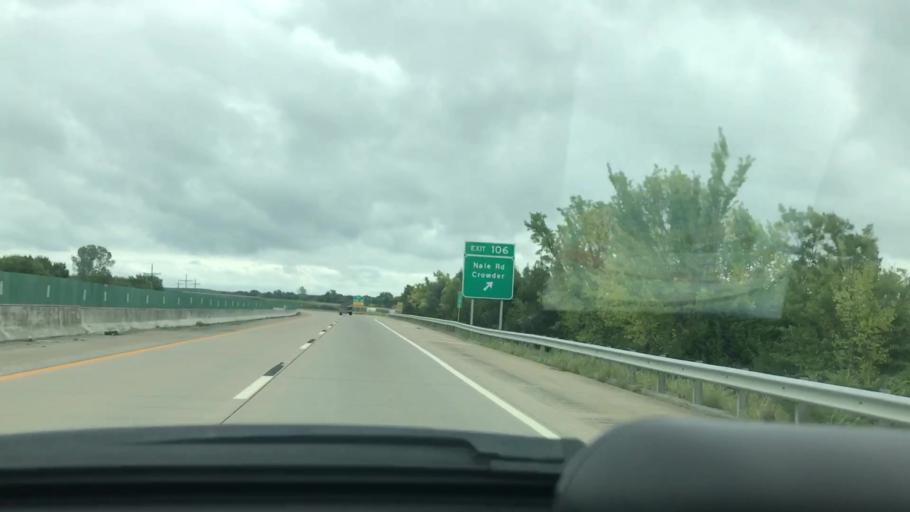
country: US
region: Oklahoma
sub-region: McIntosh County
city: Eufaula
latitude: 35.1269
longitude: -95.6760
